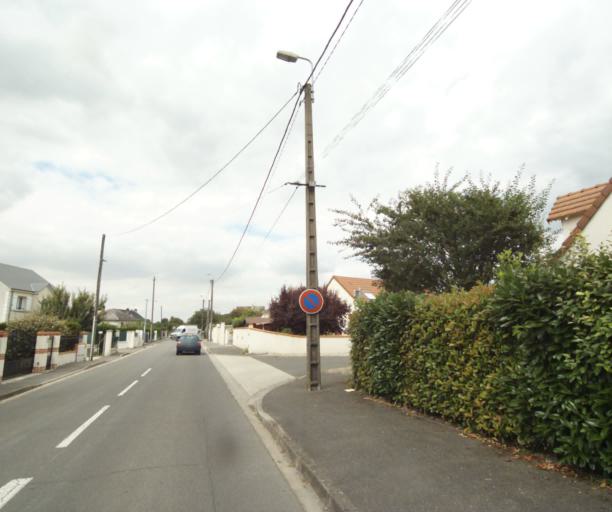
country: FR
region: Centre
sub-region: Departement du Loiret
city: Saran
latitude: 47.9394
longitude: 1.8695
